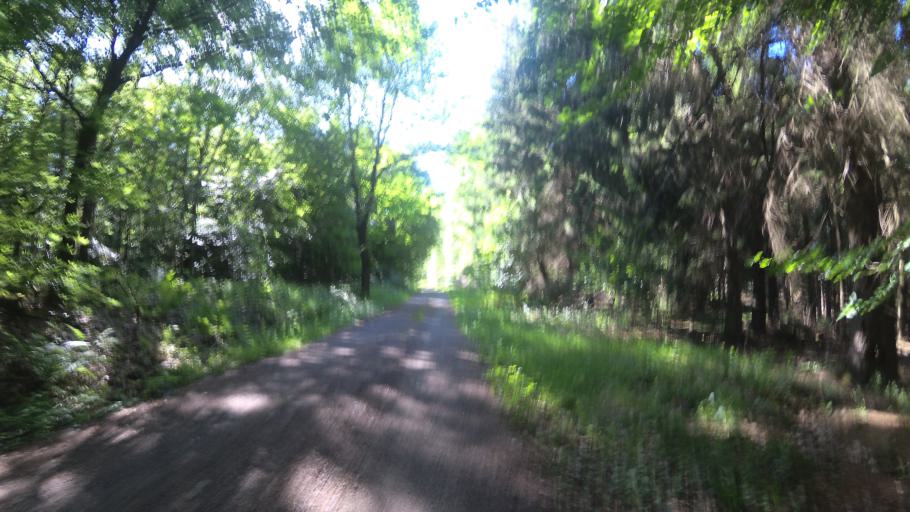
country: DE
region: Saarland
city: Mainzweiler
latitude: 49.4495
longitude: 7.1085
